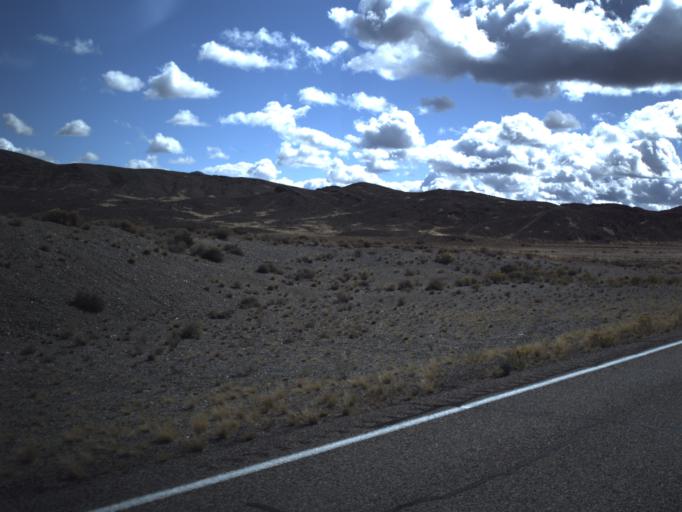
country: US
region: Nevada
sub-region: White Pine County
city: McGill
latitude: 38.9132
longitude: -114.0261
